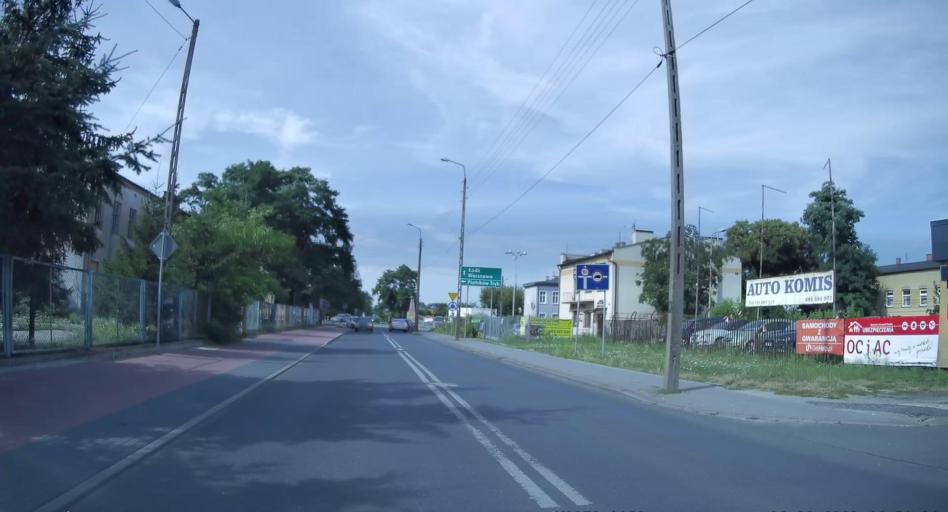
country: PL
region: Lodz Voivodeship
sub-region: Powiat tomaszowski
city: Tomaszow Mazowiecki
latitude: 51.5297
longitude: 19.9969
